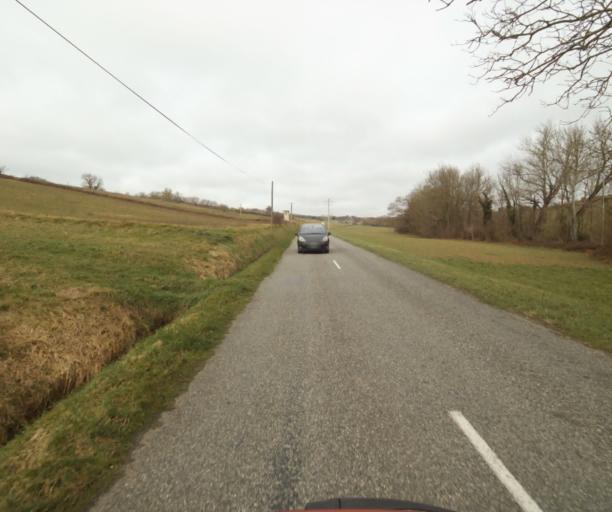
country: FR
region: Midi-Pyrenees
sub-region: Departement de l'Ariege
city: Pamiers
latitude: 43.1347
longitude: 1.5409
